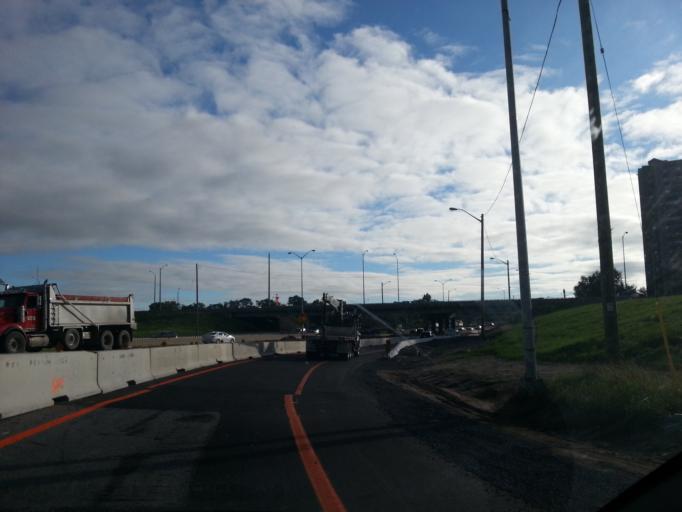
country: CA
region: Ontario
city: Ottawa
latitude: 45.4153
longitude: -75.6749
